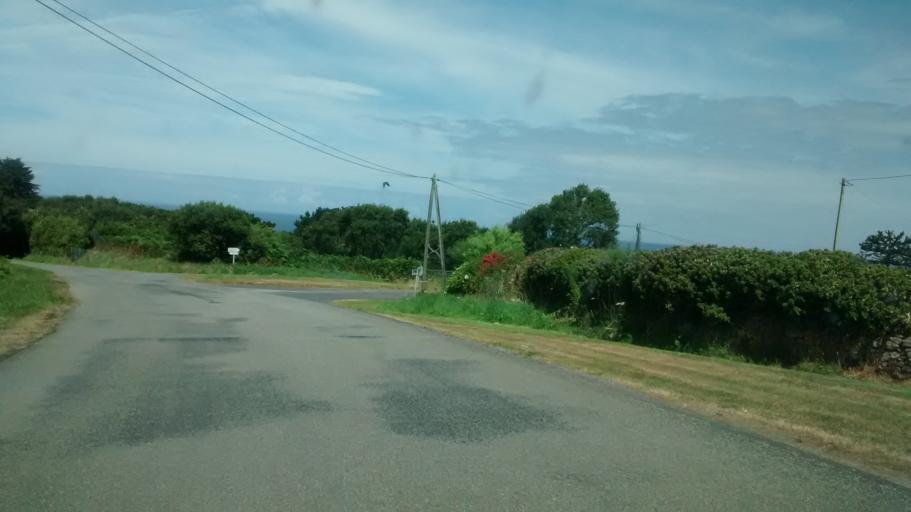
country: FR
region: Brittany
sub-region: Departement du Finistere
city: Plouguerneau
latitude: 48.6208
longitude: -4.4797
